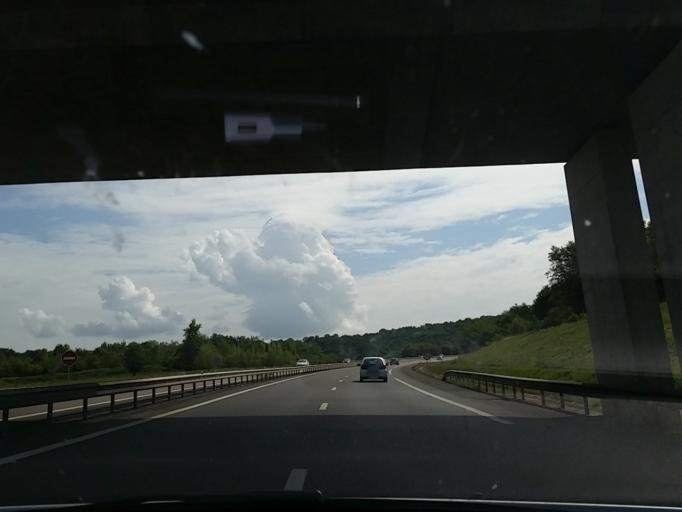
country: FR
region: Auvergne
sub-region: Departement de l'Allier
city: Vallon-en-Sully
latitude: 46.5097
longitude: 2.6301
